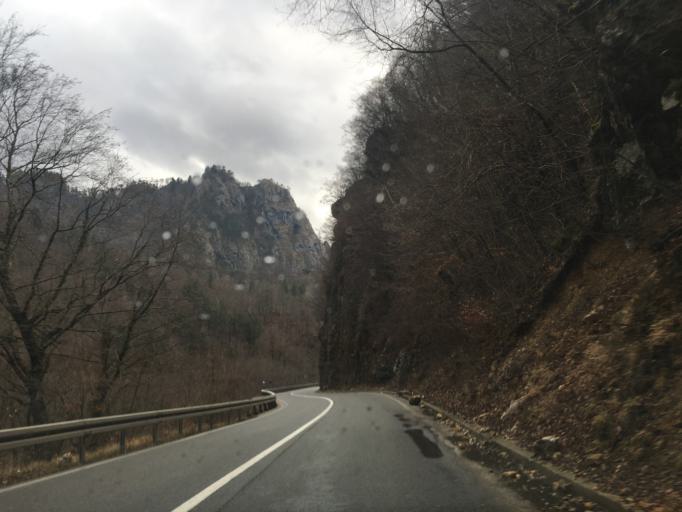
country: RS
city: Sokolovo Brdo
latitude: 43.1925
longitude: 19.7692
